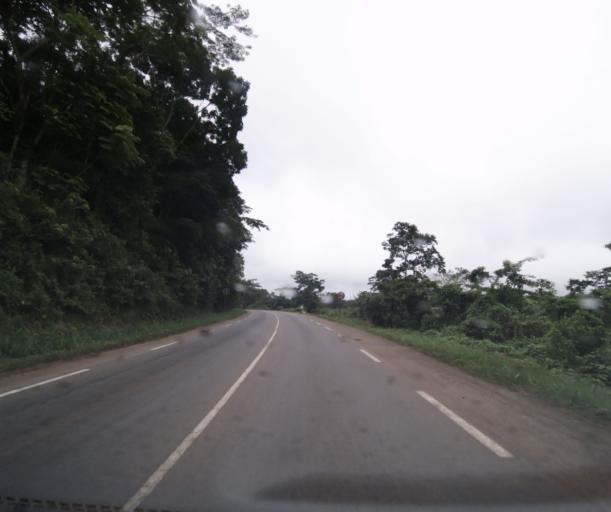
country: CM
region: Centre
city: Mbankomo
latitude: 3.7740
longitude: 11.1512
